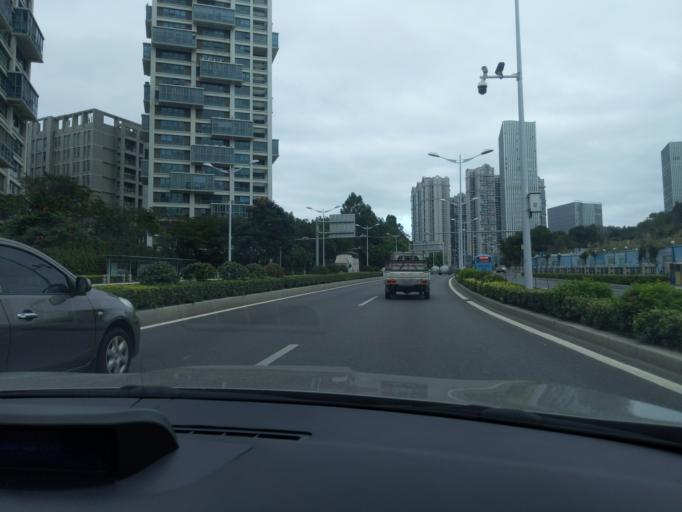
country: CN
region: Fujian
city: Liuwudian
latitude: 24.4905
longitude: 118.1833
